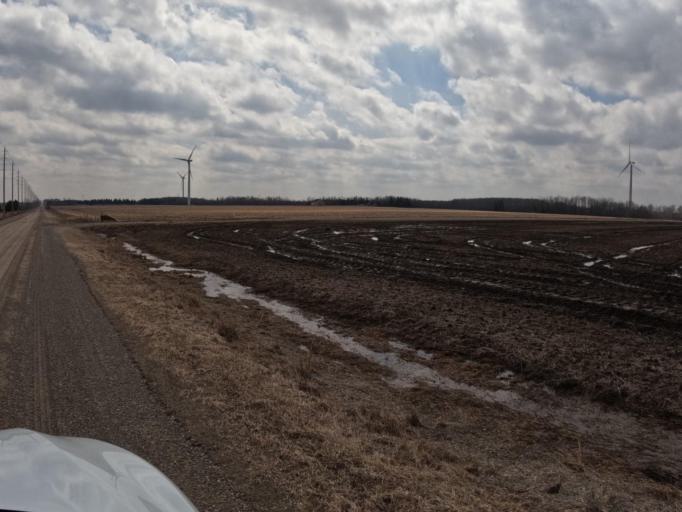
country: CA
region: Ontario
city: Shelburne
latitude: 44.0398
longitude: -80.3174
